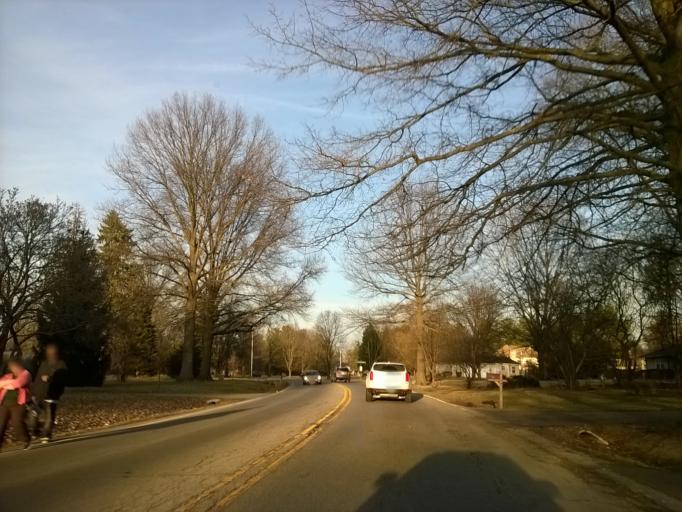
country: US
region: Indiana
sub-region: Marion County
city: Meridian Hills
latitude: 39.8559
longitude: -86.1910
